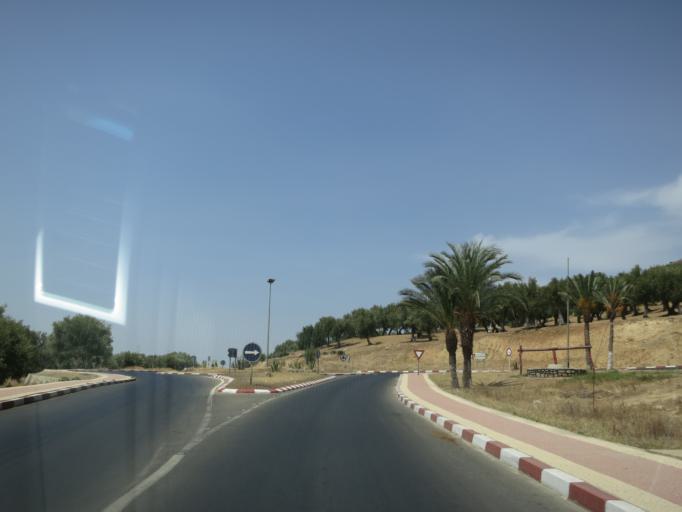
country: MA
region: Meknes-Tafilalet
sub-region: Meknes
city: Meknes
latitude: 34.0586
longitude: -5.5326
